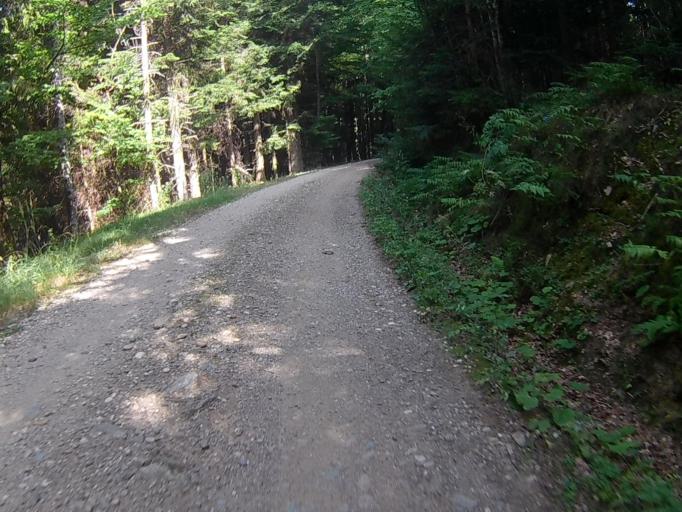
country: SI
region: Ruse
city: Ruse
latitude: 46.5157
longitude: 15.5421
